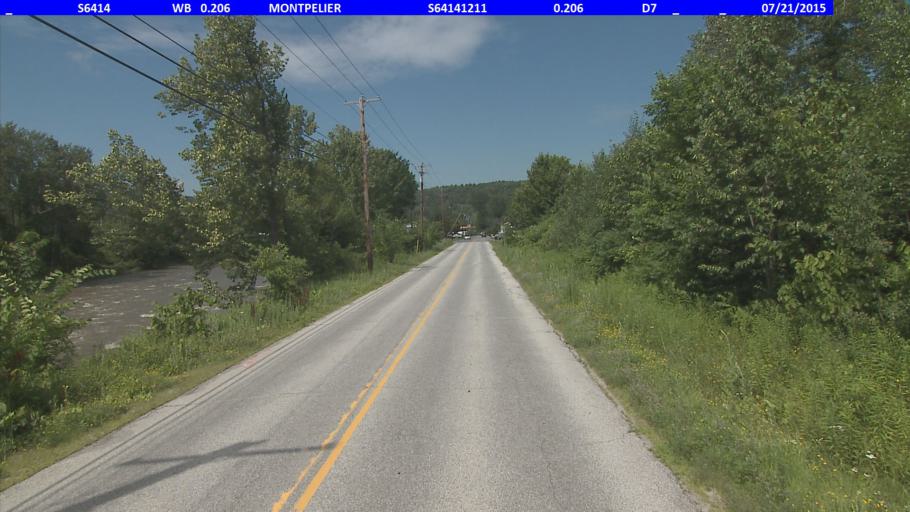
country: US
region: Vermont
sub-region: Washington County
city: Montpelier
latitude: 44.2428
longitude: -72.5408
